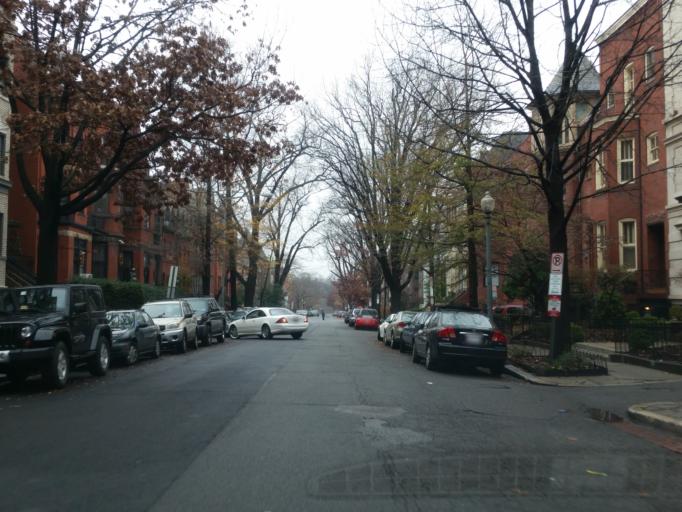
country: US
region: Washington, D.C.
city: Washington, D.C.
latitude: 38.9087
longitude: -77.0451
